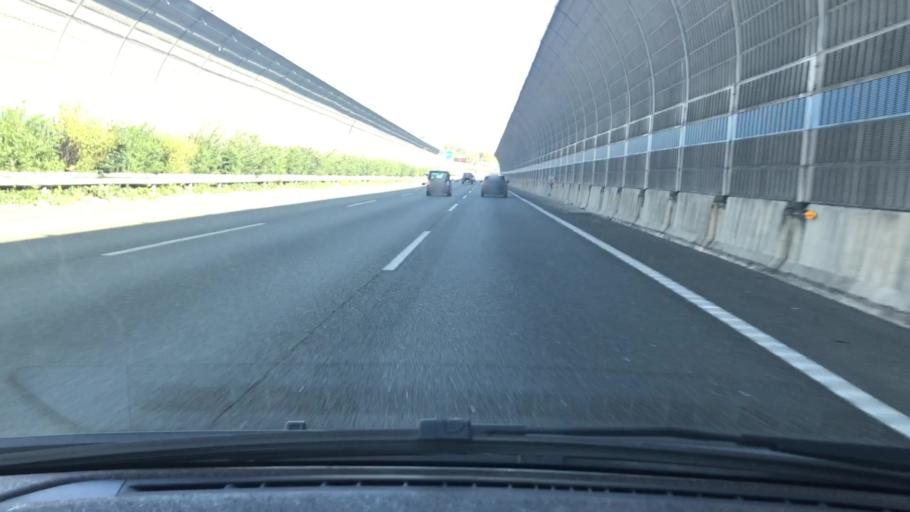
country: JP
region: Osaka
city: Ibaraki
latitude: 34.8461
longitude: 135.5765
